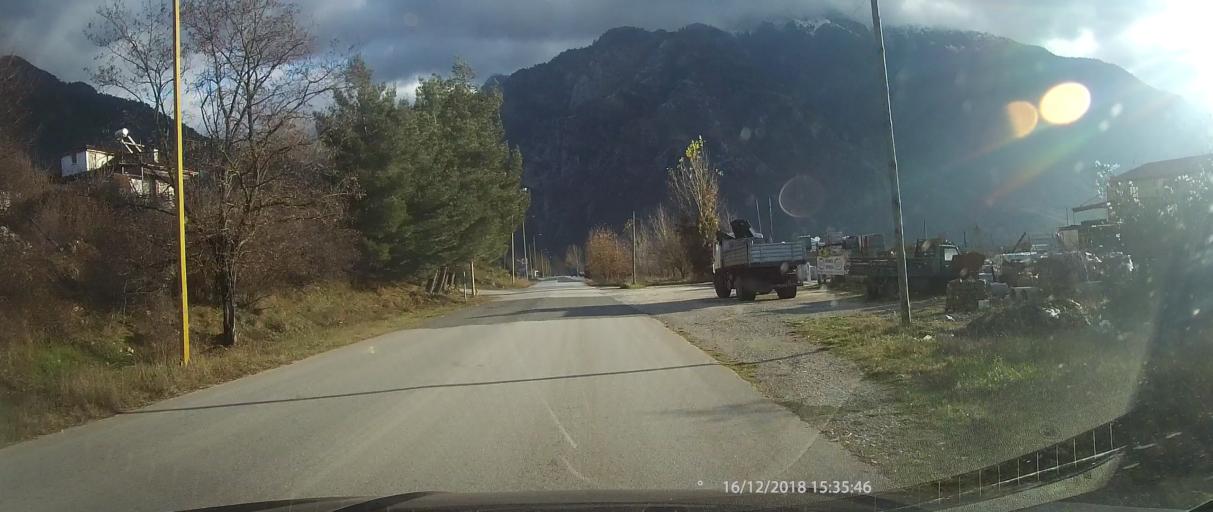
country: GR
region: Epirus
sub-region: Nomos Ioanninon
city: Konitsa
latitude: 40.0473
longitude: 20.7389
